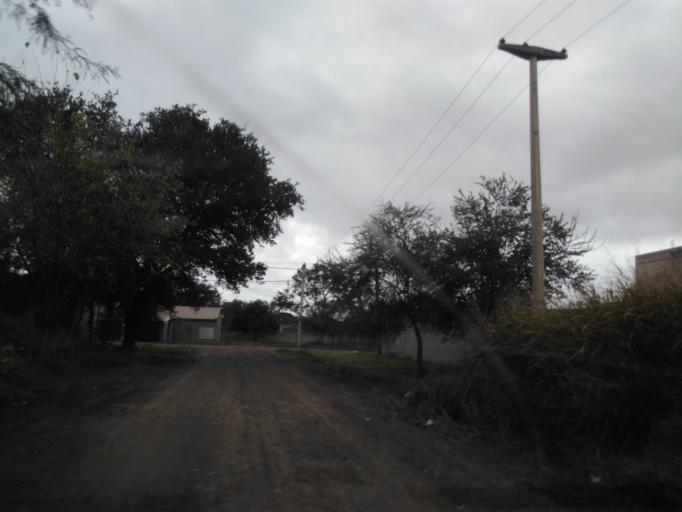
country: AR
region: Chaco
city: Fontana
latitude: -27.4500
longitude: -59.0317
